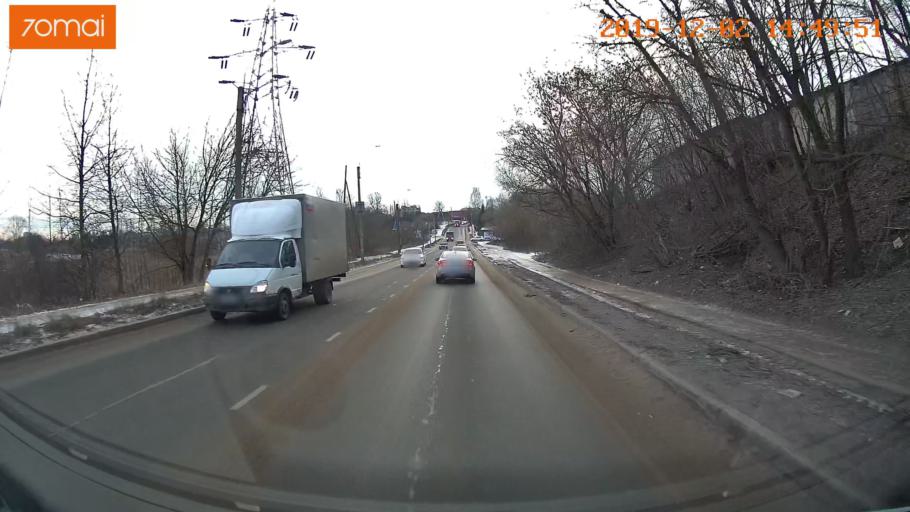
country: RU
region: Ivanovo
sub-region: Gorod Ivanovo
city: Ivanovo
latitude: 56.9844
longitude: 41.0088
